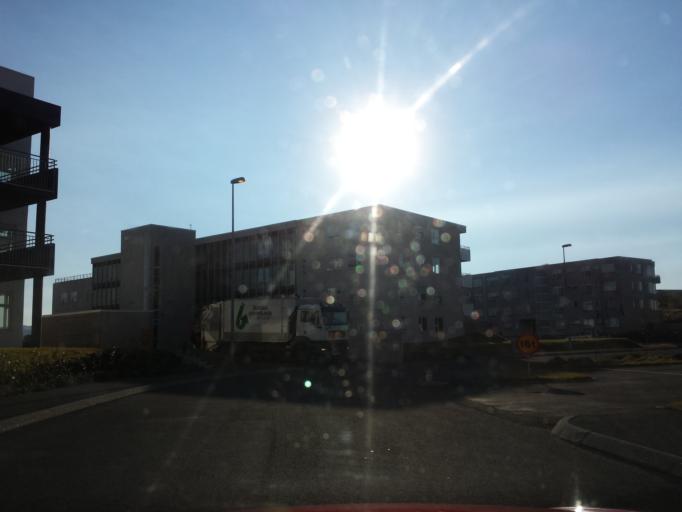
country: IS
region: Capital Region
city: Reykjavik
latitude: 64.0831
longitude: -21.8200
